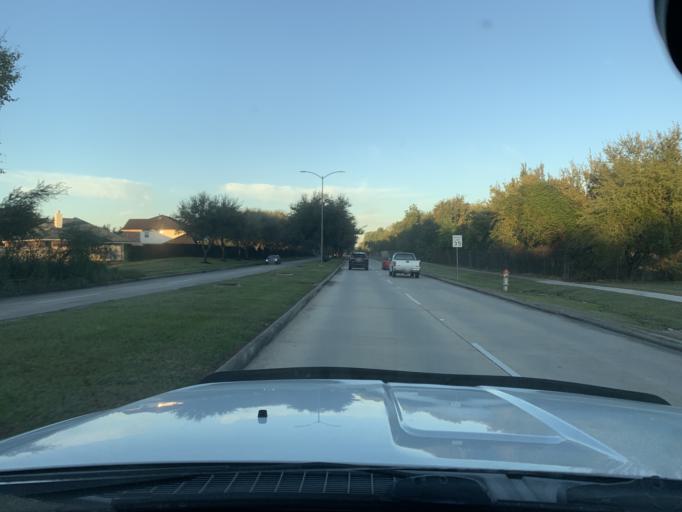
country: US
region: Texas
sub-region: Fort Bend County
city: Sugar Land
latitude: 29.6512
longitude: -95.6251
